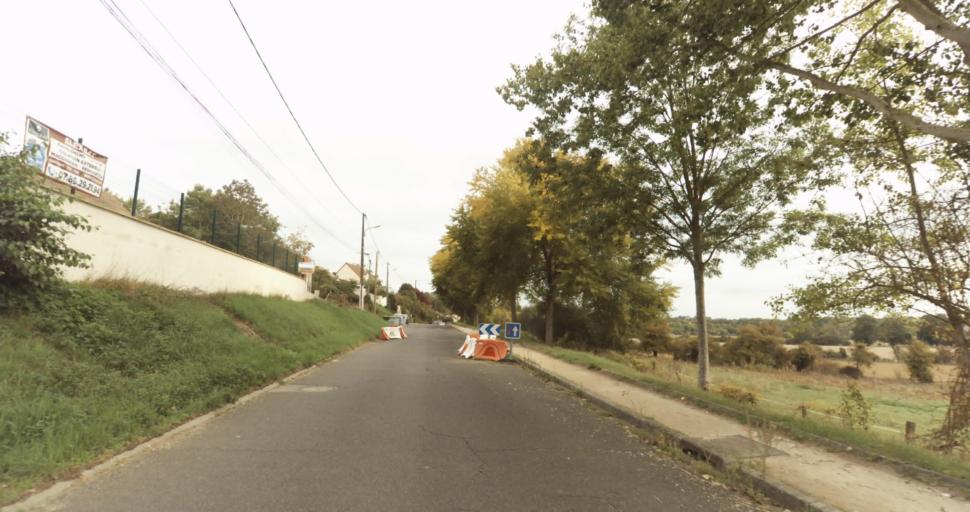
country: FR
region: Centre
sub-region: Departement d'Eure-et-Loir
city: Dreux
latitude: 48.7234
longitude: 1.3493
